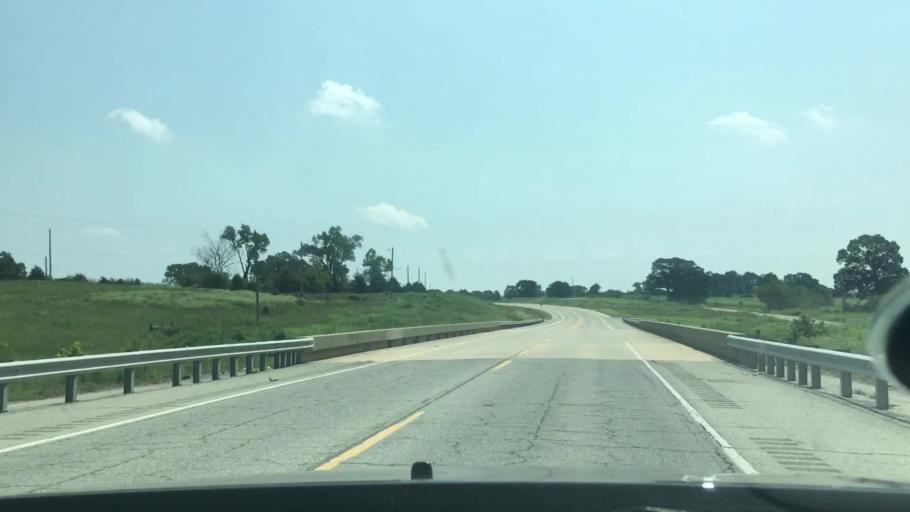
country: US
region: Oklahoma
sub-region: Atoka County
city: Atoka
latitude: 34.2914
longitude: -95.9729
